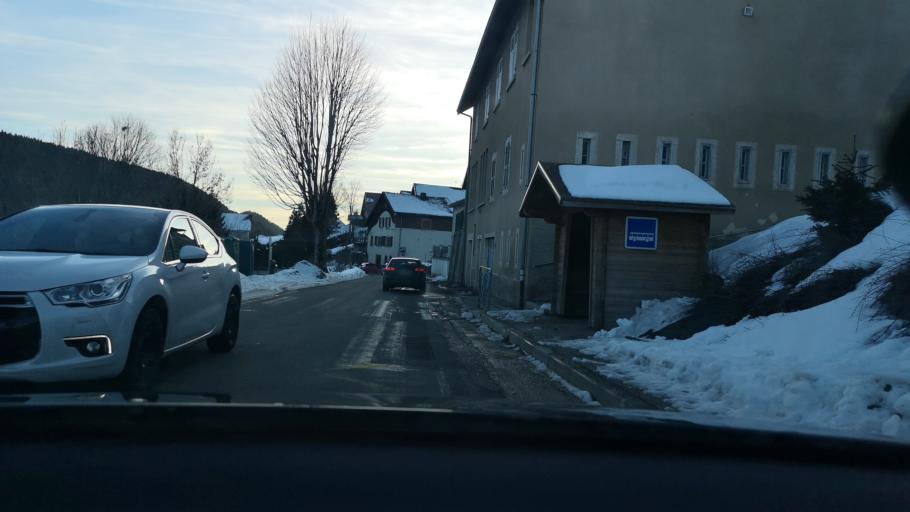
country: FR
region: Franche-Comte
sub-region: Departement du Doubs
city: La Cluse-et-Mijoux
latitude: 46.9382
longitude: 6.4253
